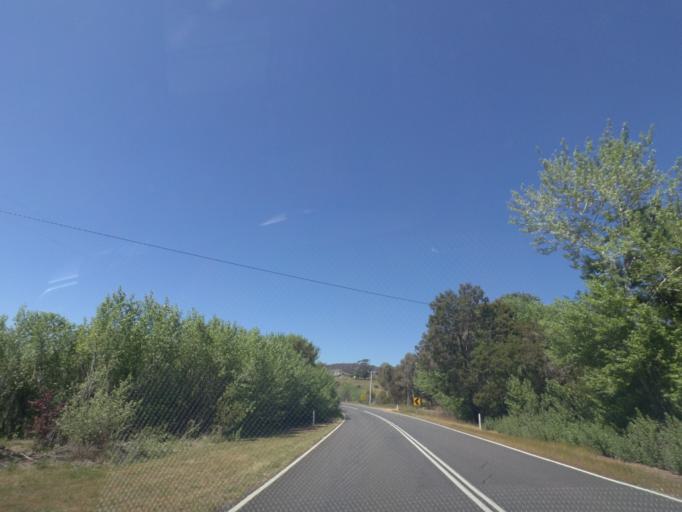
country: AU
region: Victoria
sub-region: Hume
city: Sunbury
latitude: -37.0802
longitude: 144.7667
